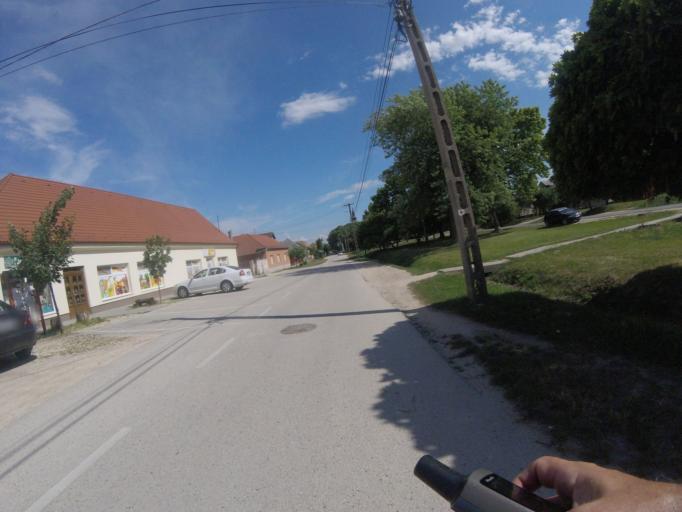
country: HU
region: Fejer
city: Szarliget
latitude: 47.4786
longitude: 18.5172
